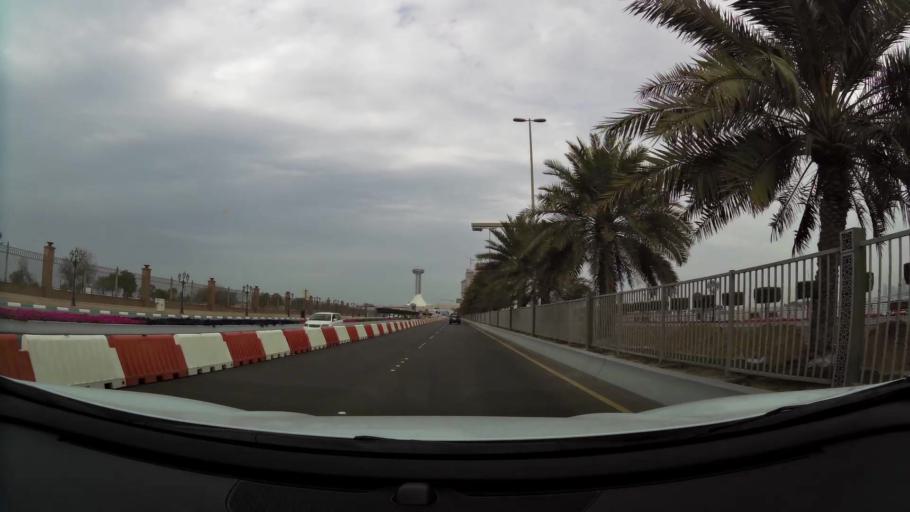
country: AE
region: Abu Dhabi
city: Abu Dhabi
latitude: 24.4669
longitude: 54.3229
